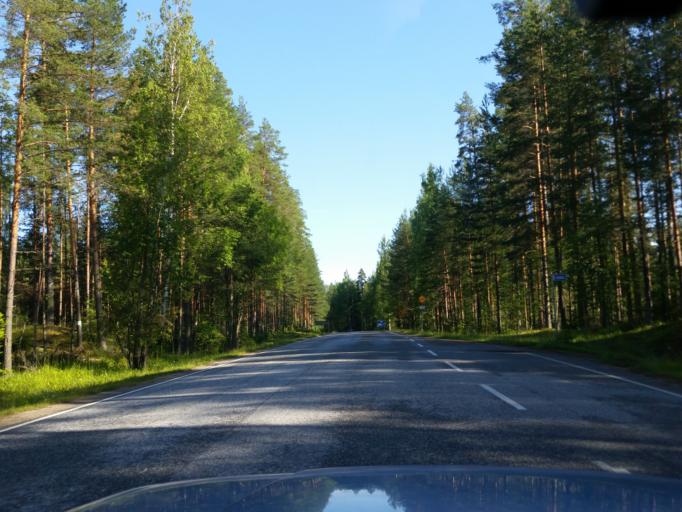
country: FI
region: Southern Savonia
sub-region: Savonlinna
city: Sulkava
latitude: 61.7992
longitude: 28.4140
